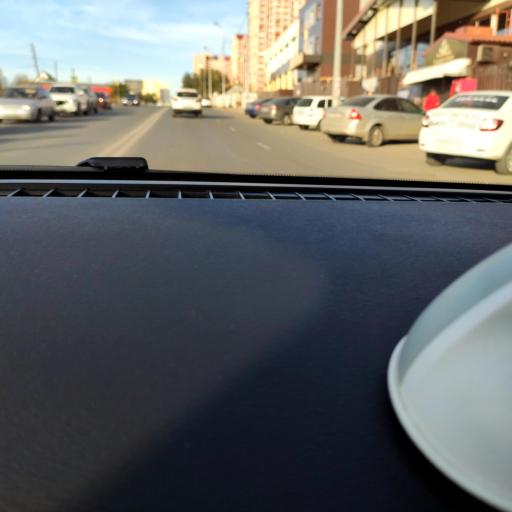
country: RU
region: Samara
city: Samara
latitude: 53.2062
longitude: 50.2126
